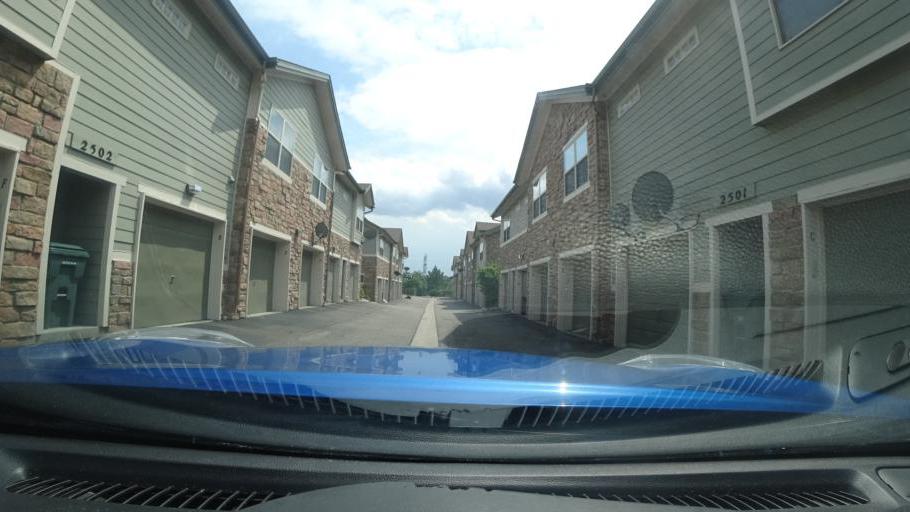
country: US
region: Colorado
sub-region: Adams County
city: Aurora
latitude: 39.6701
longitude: -104.7701
